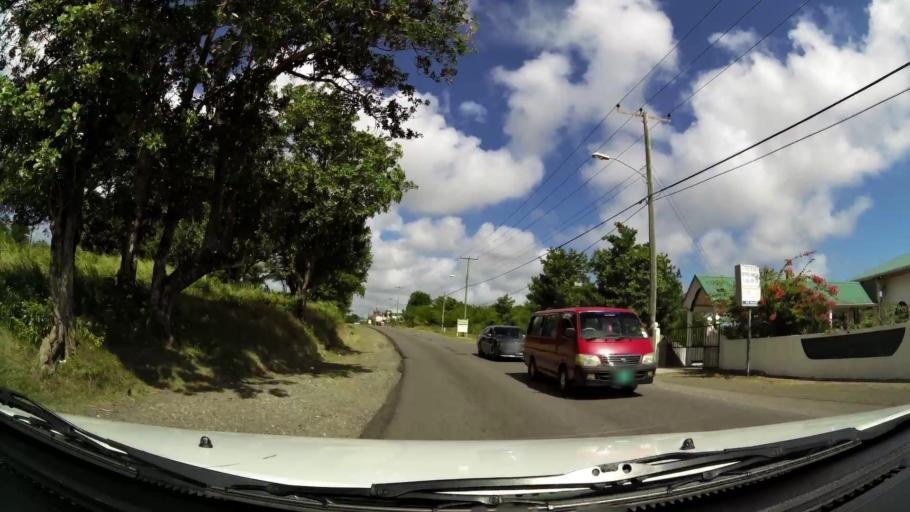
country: LC
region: Laborie Quarter
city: Laborie
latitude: 13.7441
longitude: -60.9708
